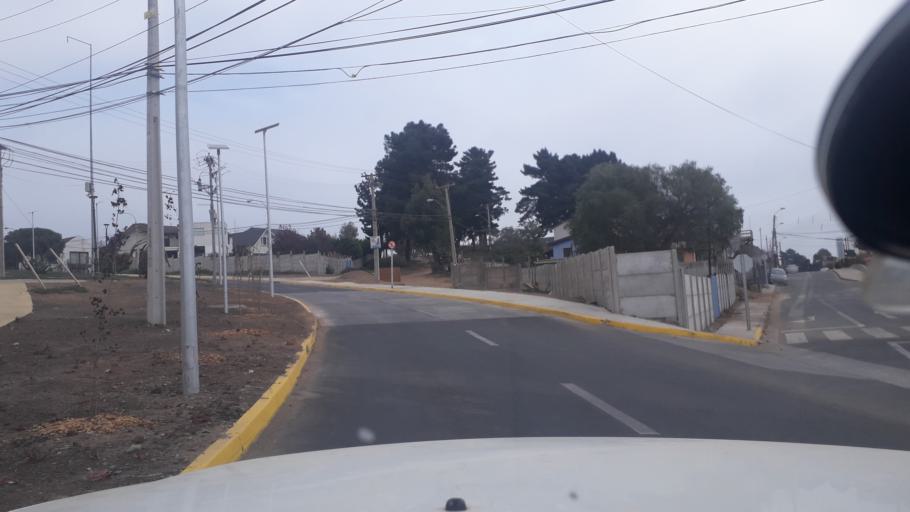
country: CL
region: Valparaiso
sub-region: Provincia de Valparaiso
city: Vina del Mar
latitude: -32.9382
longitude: -71.5365
